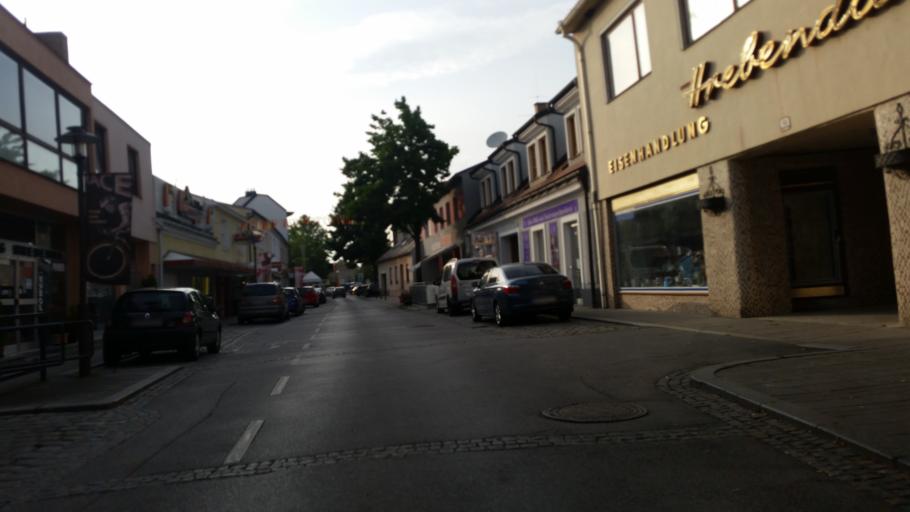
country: AT
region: Lower Austria
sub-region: Politischer Bezirk Mistelbach
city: Wolkersdorf im Weinviertel
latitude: 48.3841
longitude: 16.5168
